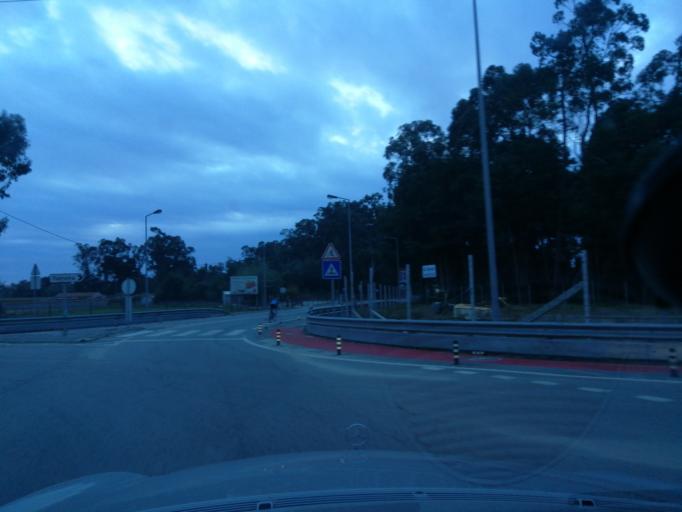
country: PT
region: Aveiro
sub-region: Murtosa
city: Murtosa
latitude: 40.7620
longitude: -8.6239
